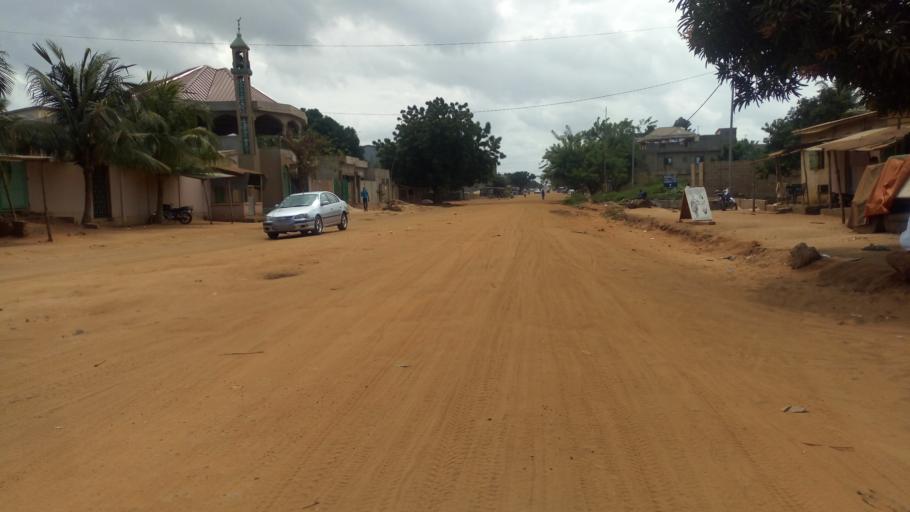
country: TG
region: Maritime
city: Lome
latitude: 6.2215
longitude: 1.1810
